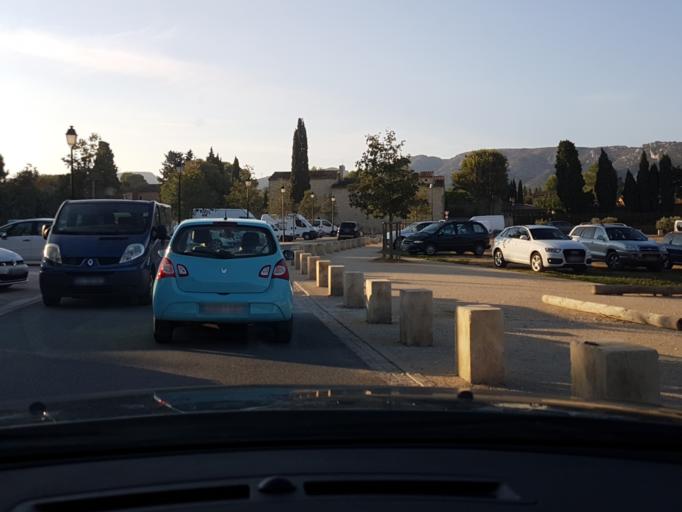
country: FR
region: Provence-Alpes-Cote d'Azur
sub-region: Departement des Bouches-du-Rhone
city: Eygalieres
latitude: 43.7615
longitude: 4.9482
